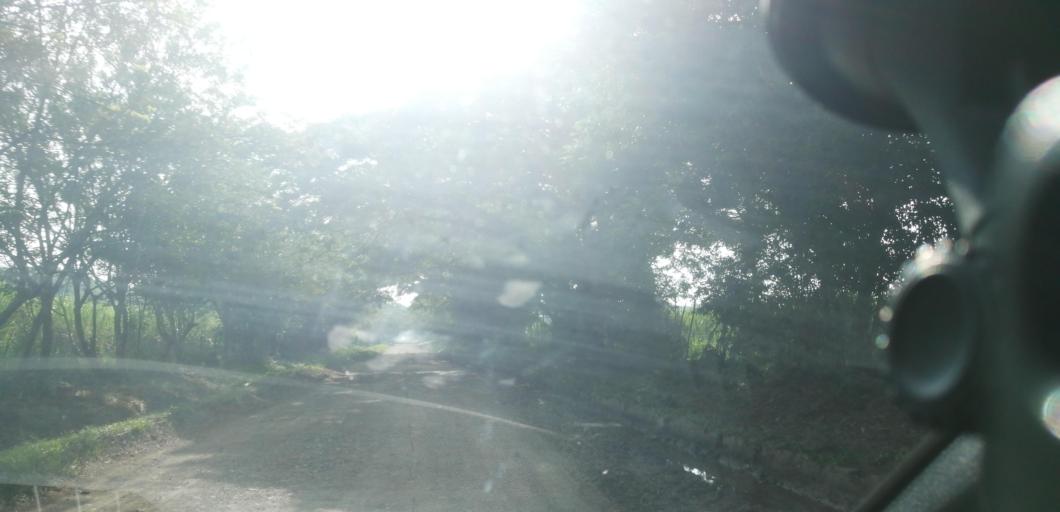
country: CO
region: Valle del Cauca
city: Yumbo
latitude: 3.5814
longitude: -76.4205
